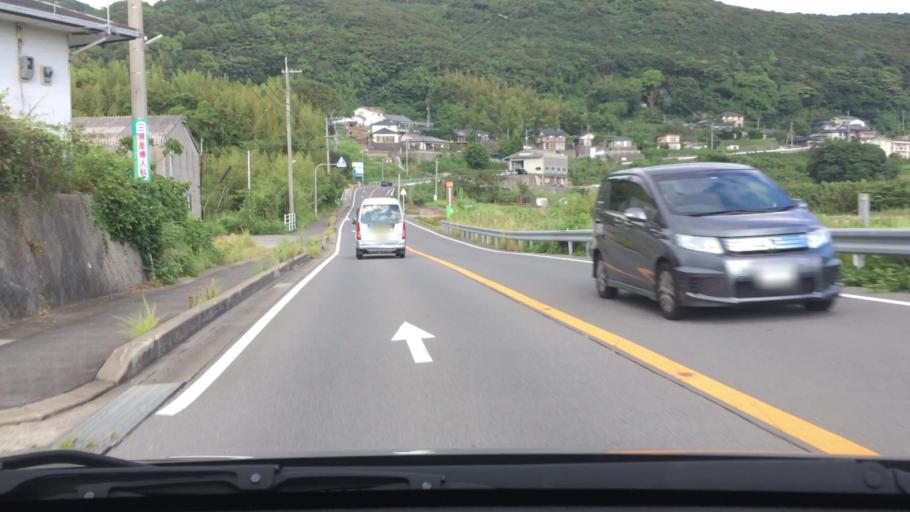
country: JP
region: Nagasaki
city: Togitsu
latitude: 32.8305
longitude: 129.7199
